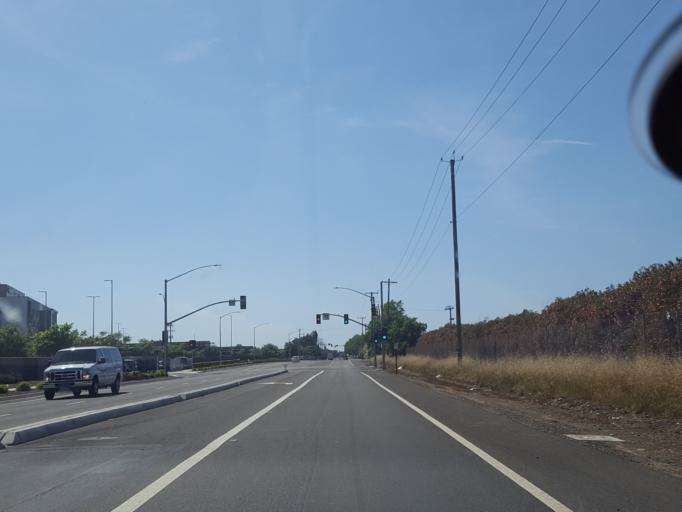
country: US
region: California
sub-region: Sacramento County
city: Rosemont
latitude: 38.5431
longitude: -121.3299
